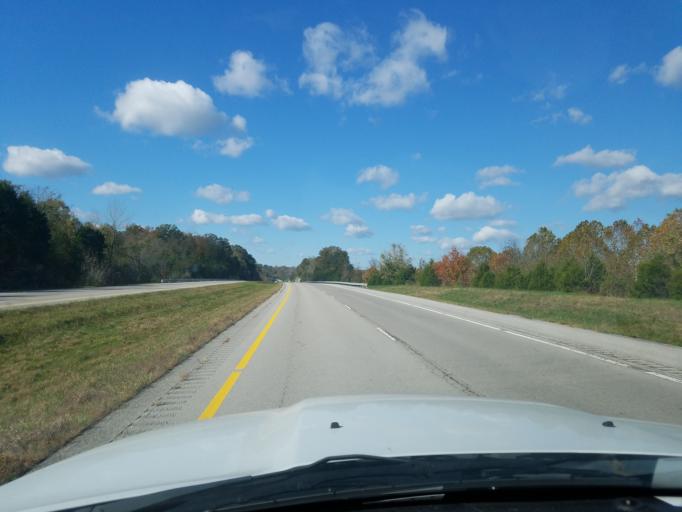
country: US
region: Kentucky
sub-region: Metcalfe County
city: Edmonton
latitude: 37.0288
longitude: -85.5257
